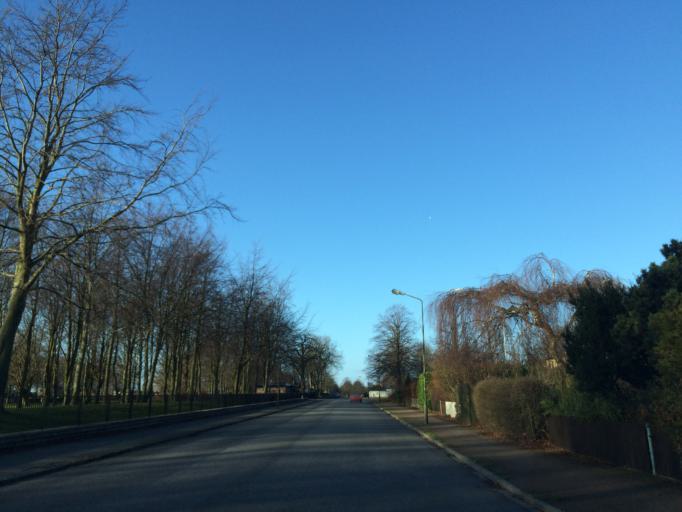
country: SE
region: Skane
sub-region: Malmo
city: Bunkeflostrand
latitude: 55.5748
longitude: 12.9492
